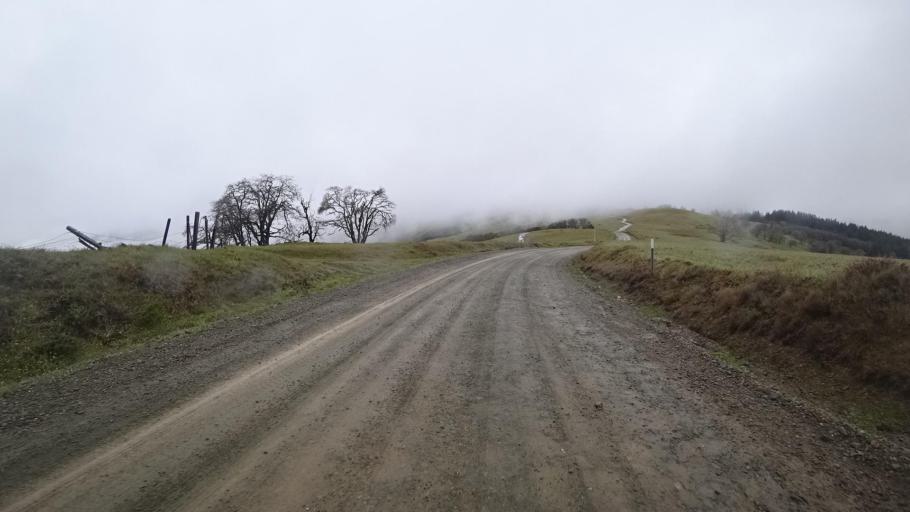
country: US
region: California
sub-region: Humboldt County
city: Westhaven-Moonstone
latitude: 41.1412
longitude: -123.8628
